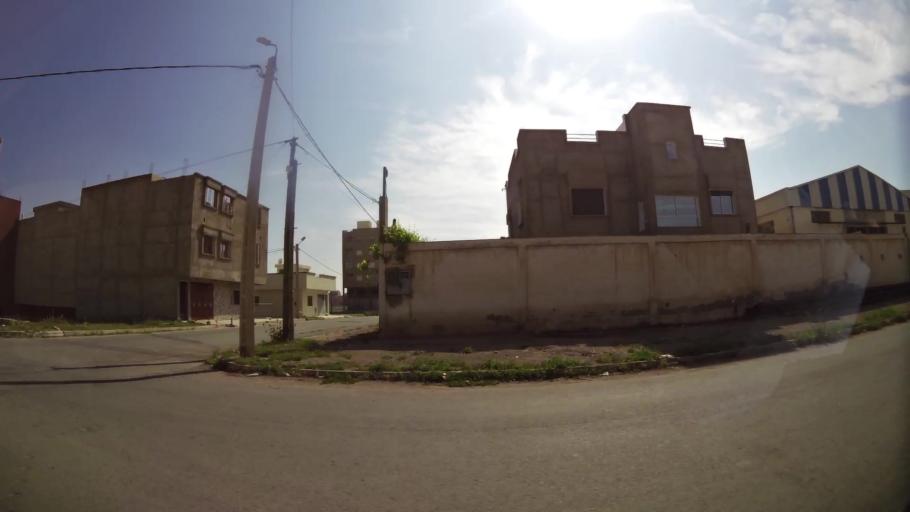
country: MA
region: Oriental
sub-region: Oujda-Angad
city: Oujda
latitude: 34.7019
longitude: -1.8850
